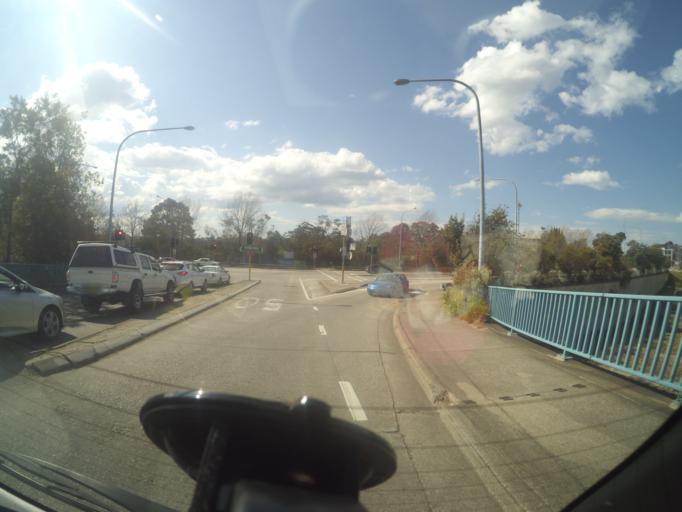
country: AU
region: New South Wales
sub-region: Blue Mountains Municipality
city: Katoomba
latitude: -33.7111
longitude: 150.3109
